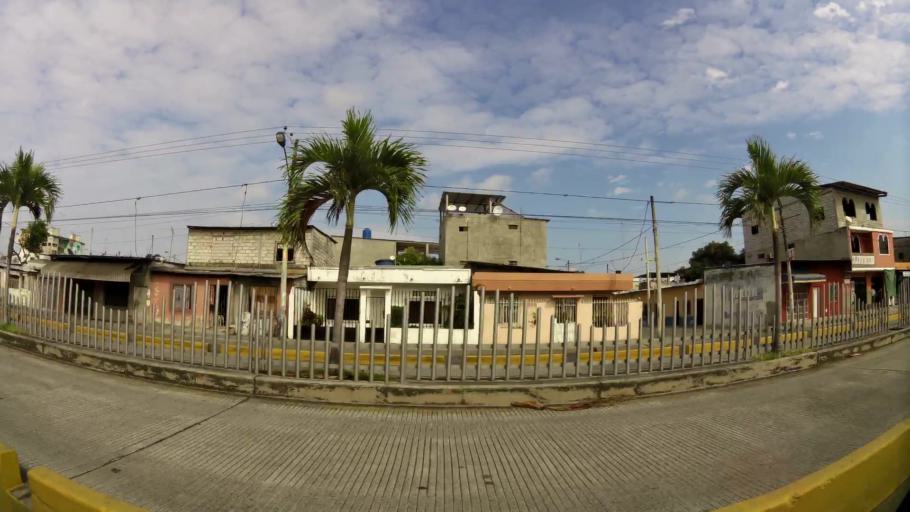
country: EC
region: Guayas
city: Guayaquil
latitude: -2.2576
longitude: -79.8790
